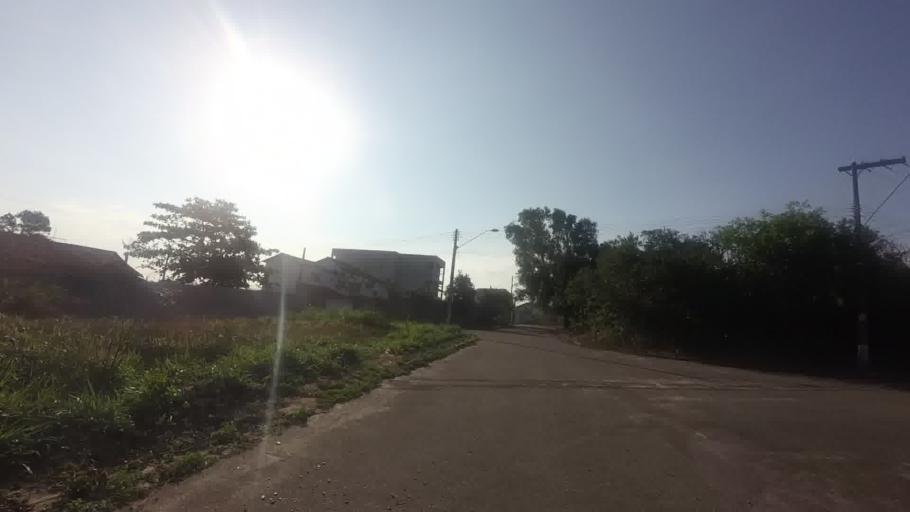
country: BR
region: Espirito Santo
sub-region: Guarapari
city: Guarapari
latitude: -20.7268
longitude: -40.5334
